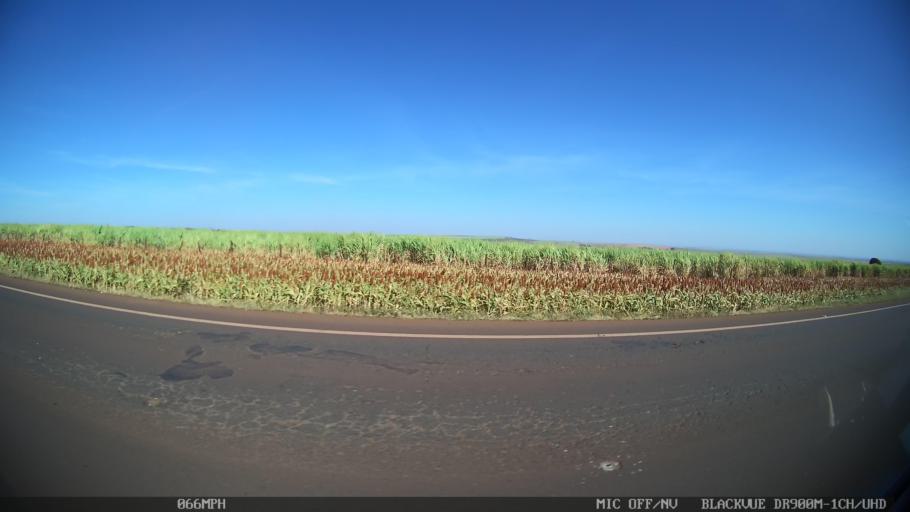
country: BR
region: Sao Paulo
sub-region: Ipua
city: Ipua
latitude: -20.4756
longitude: -48.0940
